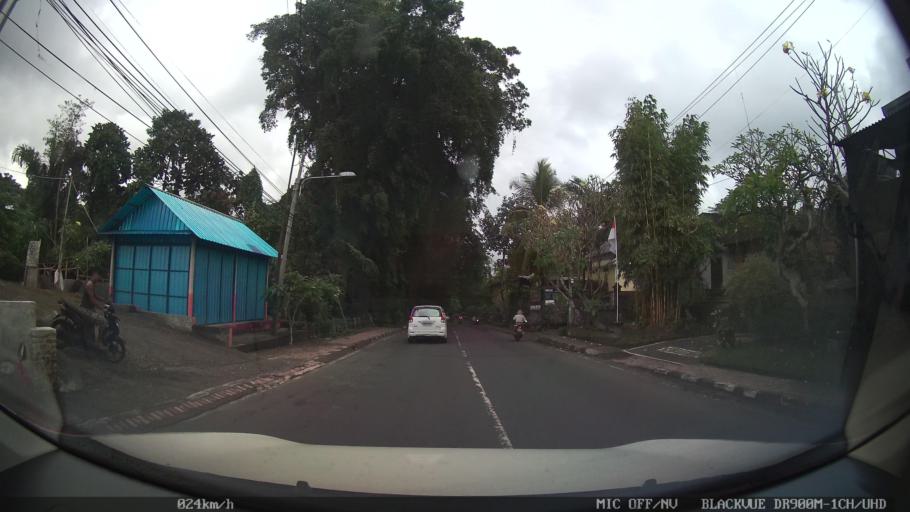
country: ID
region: Bali
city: Banjar Mambalkajanan
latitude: -8.5480
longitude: 115.2180
